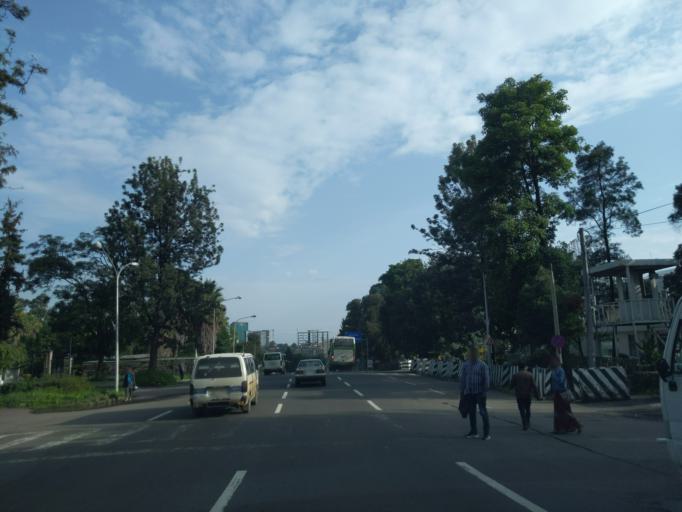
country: ET
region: Adis Abeba
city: Addis Ababa
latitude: 9.0196
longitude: 38.7634
